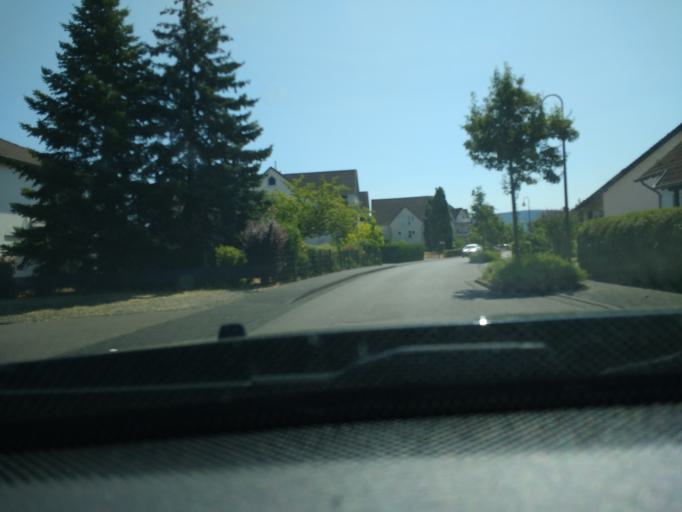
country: DE
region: Rheinland-Pfalz
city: Altrich
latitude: 49.9748
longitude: 6.9314
